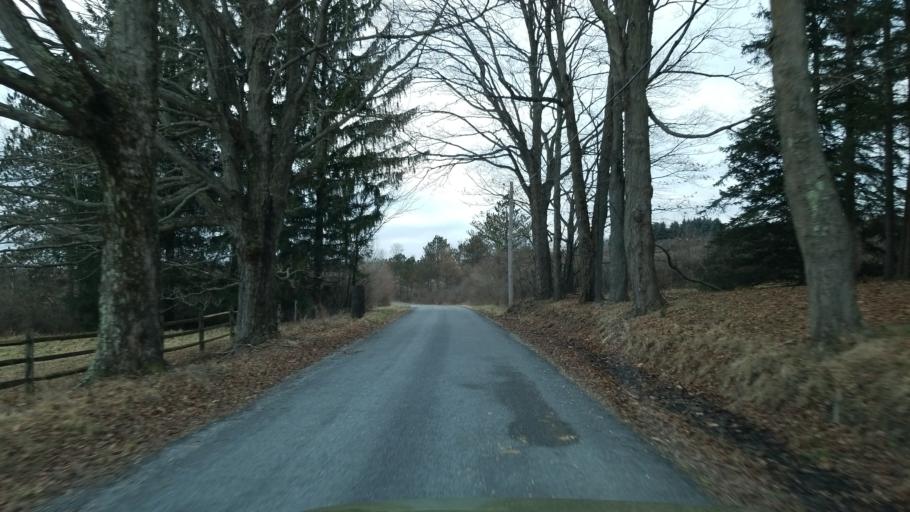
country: US
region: Pennsylvania
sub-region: Jefferson County
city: Falls Creek
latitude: 41.1809
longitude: -78.8042
